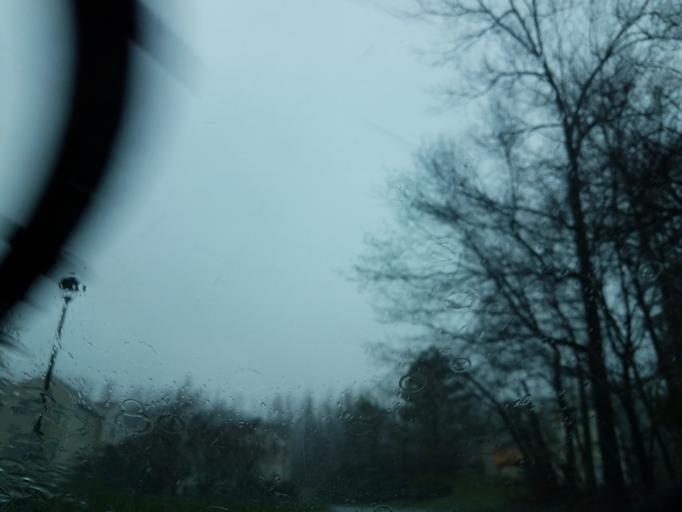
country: US
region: Connecticut
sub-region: New Haven County
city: Naugatuck
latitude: 41.5199
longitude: -73.0639
